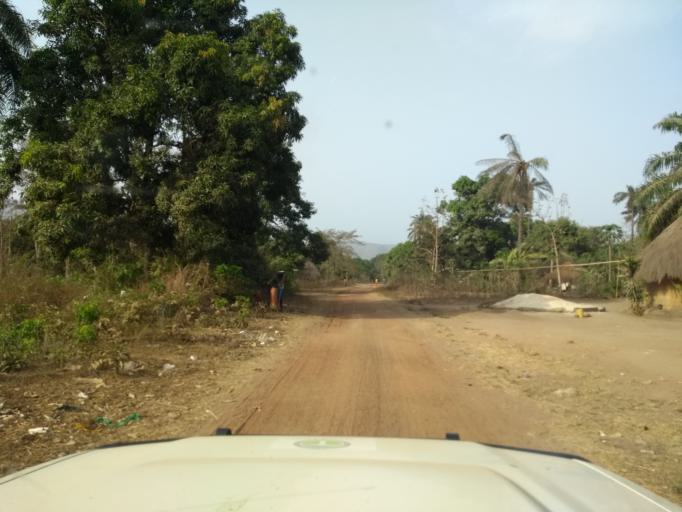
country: GN
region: Kindia
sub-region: Prefecture de Dubreka
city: Dubreka
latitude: 9.8675
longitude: -13.5428
